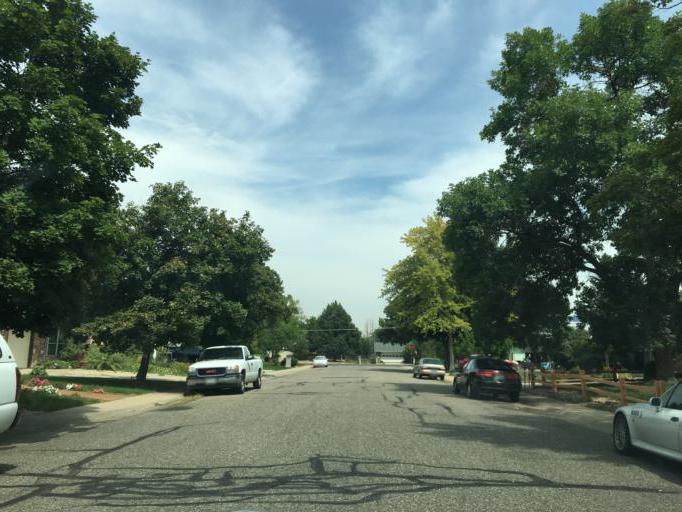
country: US
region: Colorado
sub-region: Adams County
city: Aurora
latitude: 39.7328
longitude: -104.7995
